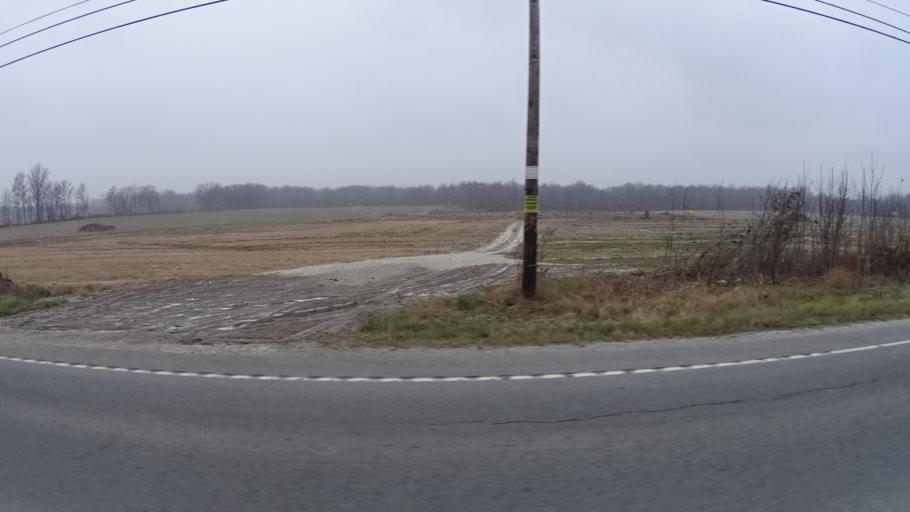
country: US
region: Ohio
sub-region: Lorain County
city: South Amherst
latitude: 41.3440
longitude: -82.2158
